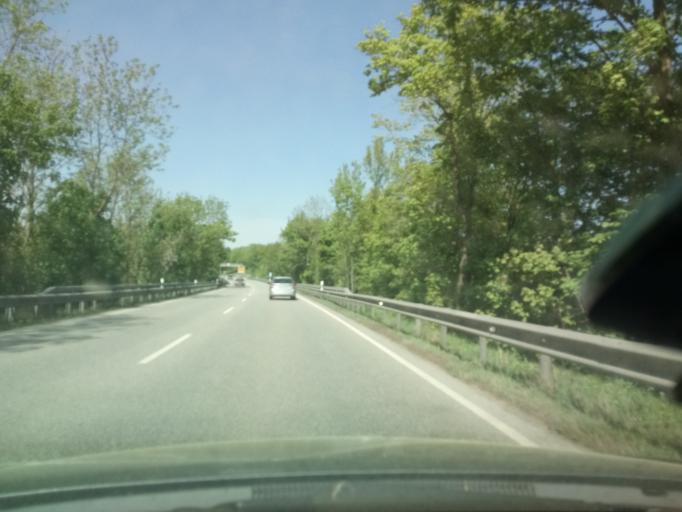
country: DE
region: Bavaria
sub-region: Upper Bavaria
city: Neuotting
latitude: 48.2343
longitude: 12.6842
